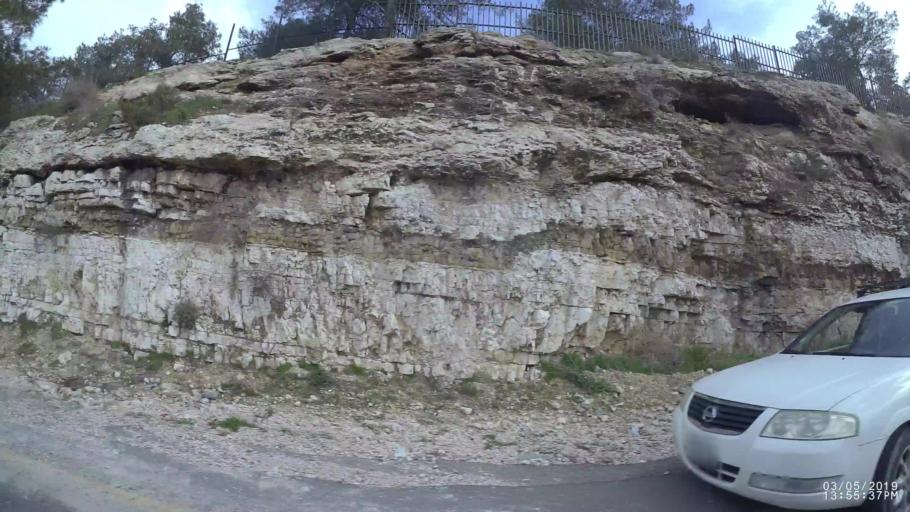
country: JO
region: Amman
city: Amman
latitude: 32.0143
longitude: 35.9349
